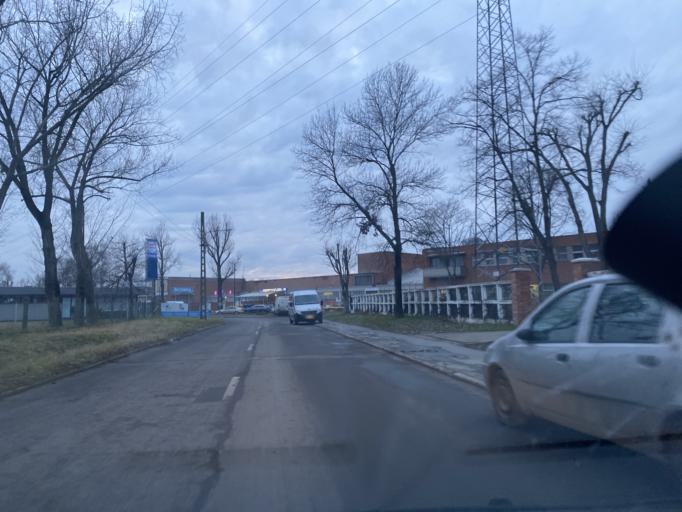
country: HU
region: Csongrad
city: Szeged
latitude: 46.2561
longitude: 20.1195
